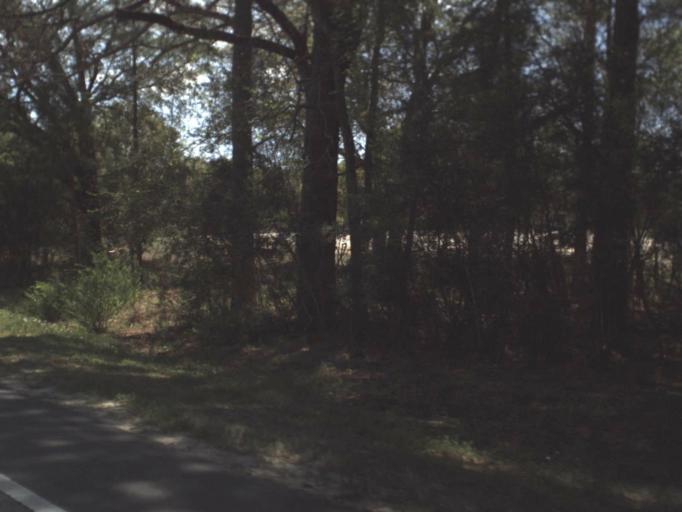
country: US
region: Alabama
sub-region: Geneva County
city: Geneva
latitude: 30.8683
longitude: -85.9457
